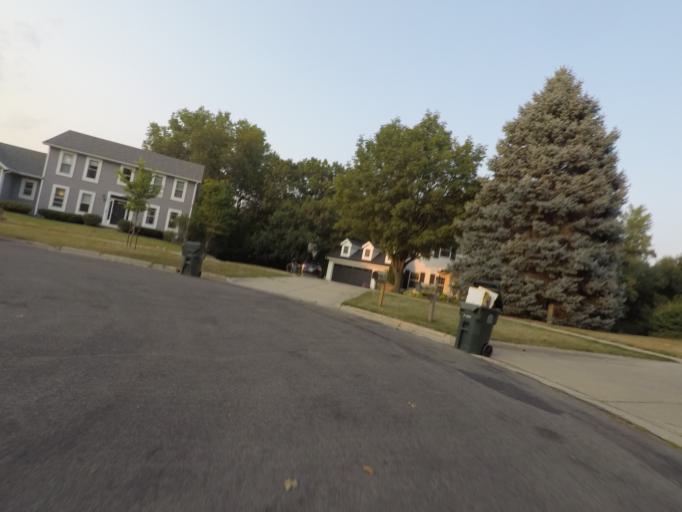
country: US
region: Wisconsin
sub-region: Dane County
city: Middleton
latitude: 43.0682
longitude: -89.5145
